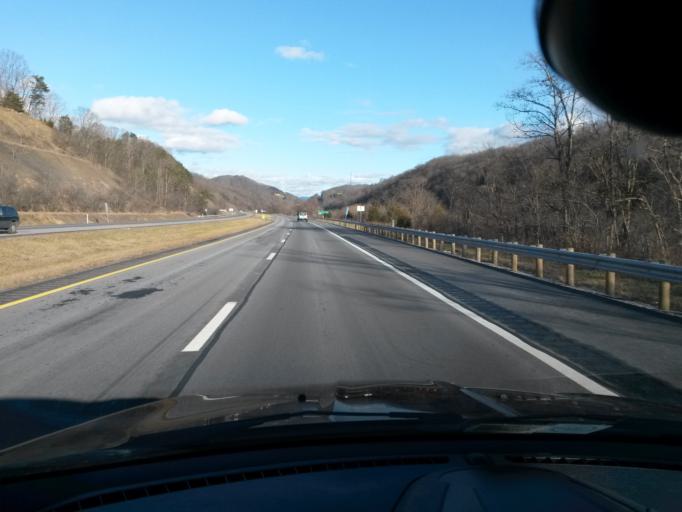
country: US
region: Virginia
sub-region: Giles County
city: Narrows
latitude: 37.3499
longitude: -80.9151
